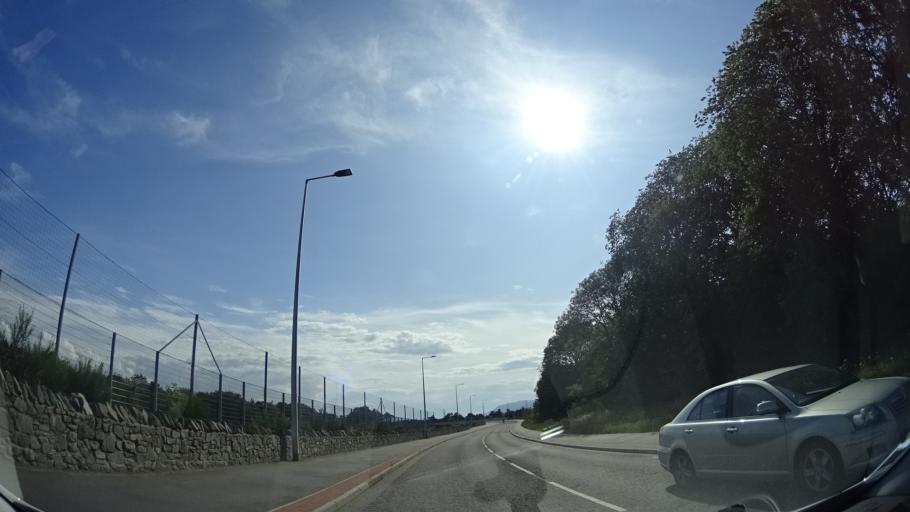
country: GB
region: Scotland
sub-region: Highland
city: Inverness
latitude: 57.4617
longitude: -4.2436
